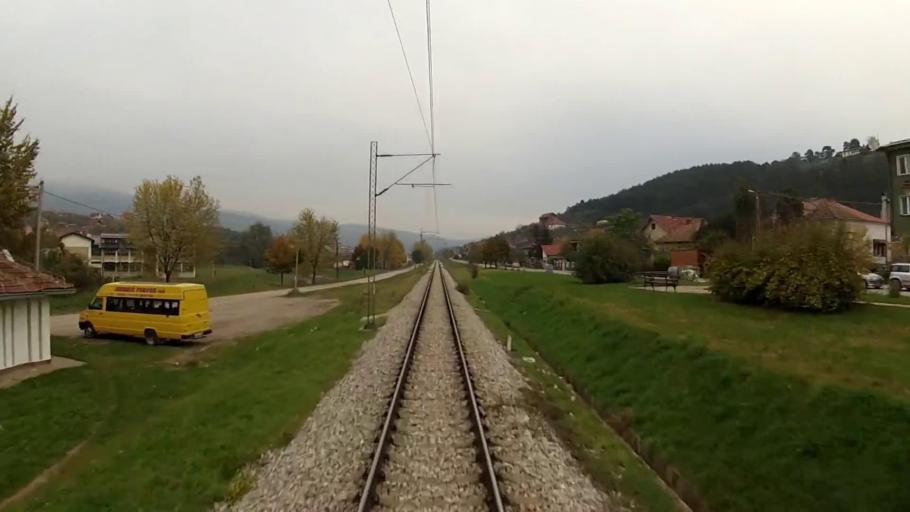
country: RS
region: Central Serbia
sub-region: Pirotski Okrug
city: Dimitrovgrad
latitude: 43.0160
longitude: 22.7894
